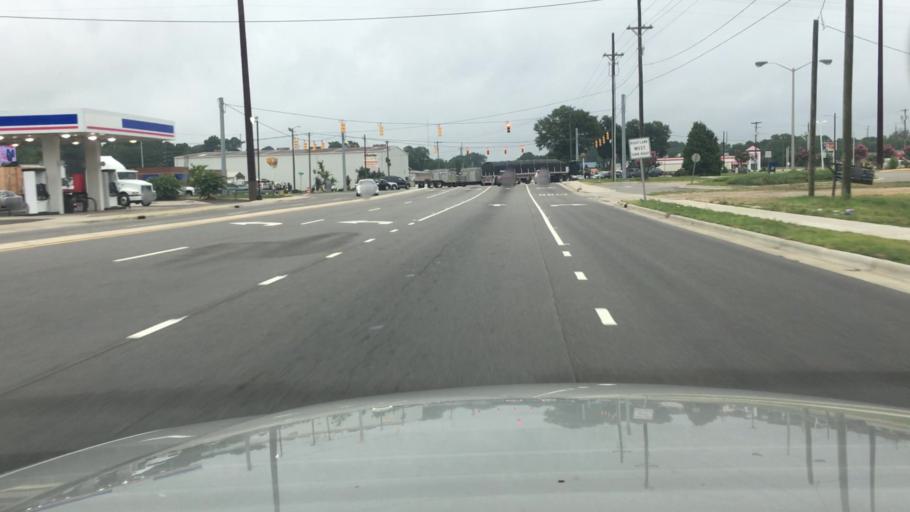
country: US
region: North Carolina
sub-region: Cumberland County
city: Fayetteville
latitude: 35.0173
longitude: -78.9049
